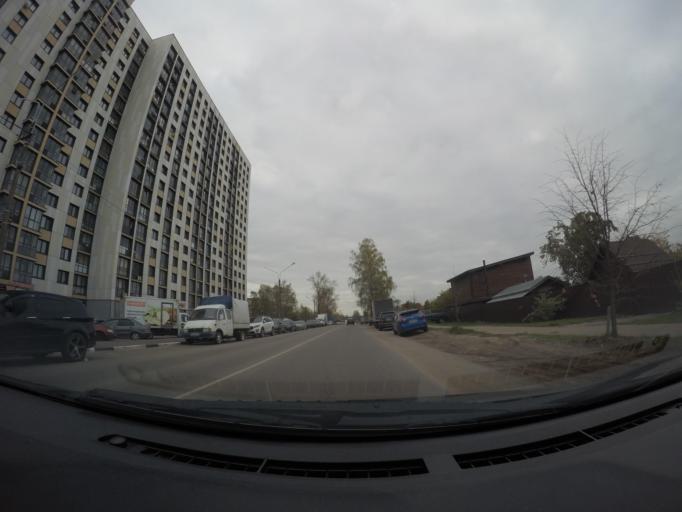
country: RU
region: Moskovskaya
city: Staraya Kupavna
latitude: 55.8020
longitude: 38.1824
